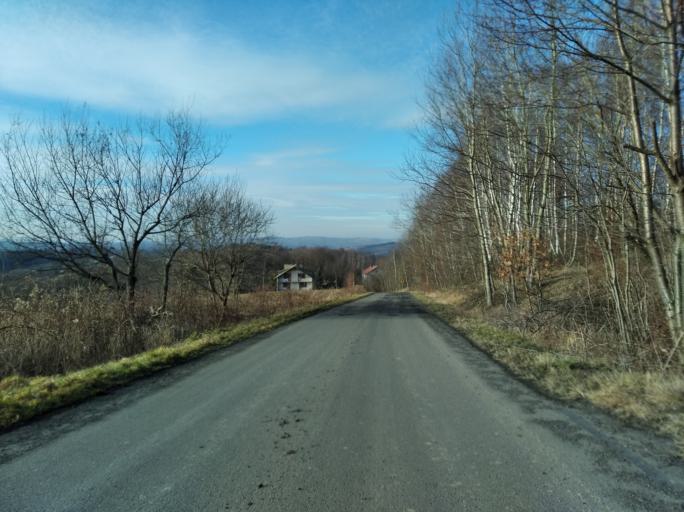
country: PL
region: Subcarpathian Voivodeship
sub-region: Powiat strzyzowski
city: Gwoznica Gorna
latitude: 49.8244
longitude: 21.9822
